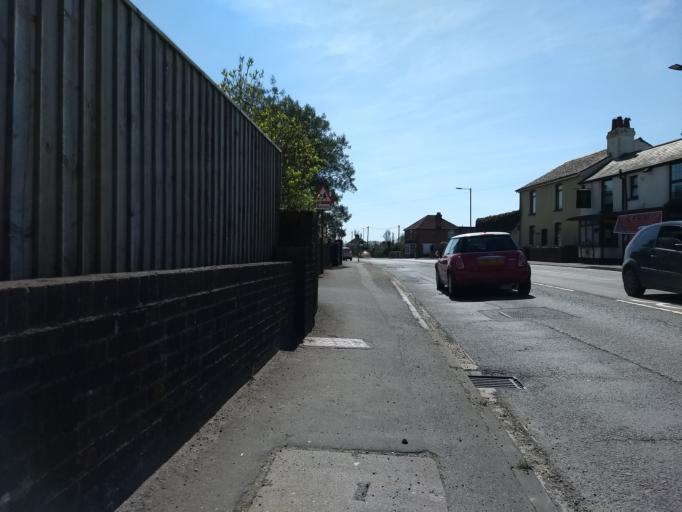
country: GB
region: England
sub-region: Isle of Wight
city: Northwood
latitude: 50.7392
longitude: -1.3077
